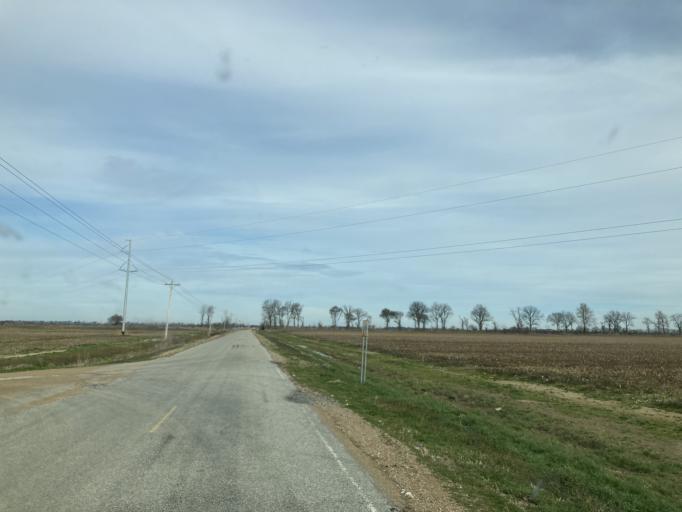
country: US
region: Mississippi
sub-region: Humphreys County
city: Belzoni
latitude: 33.0811
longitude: -90.6146
